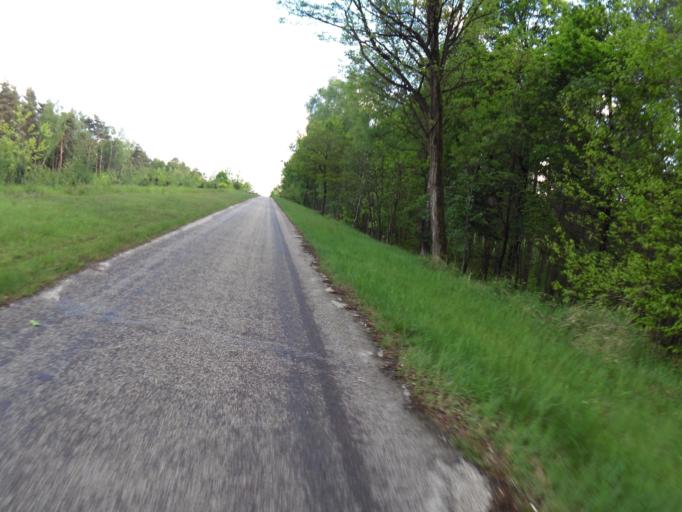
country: BE
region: Flanders
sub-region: Provincie Limburg
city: Zutendaal
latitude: 50.9647
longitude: 5.6177
